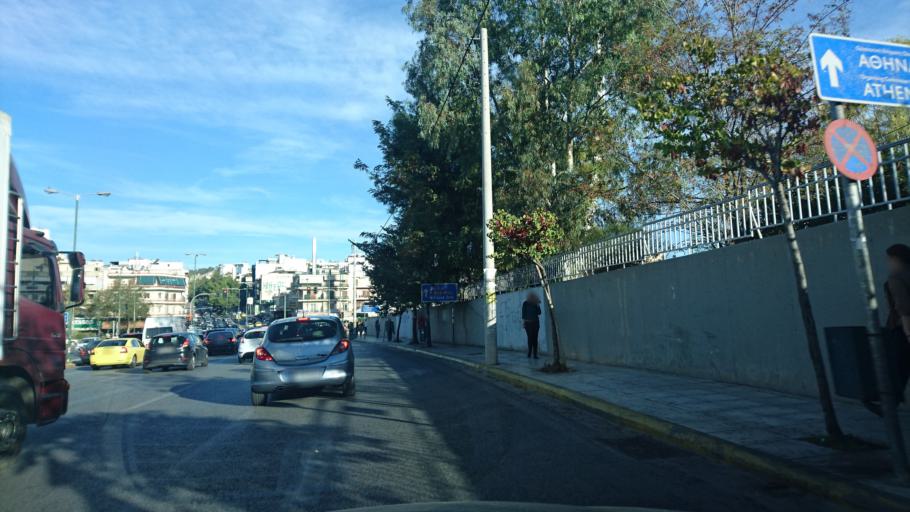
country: GR
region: Attica
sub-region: Nomarchia Athinas
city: Neo Psychiko
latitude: 37.9923
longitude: 23.7768
